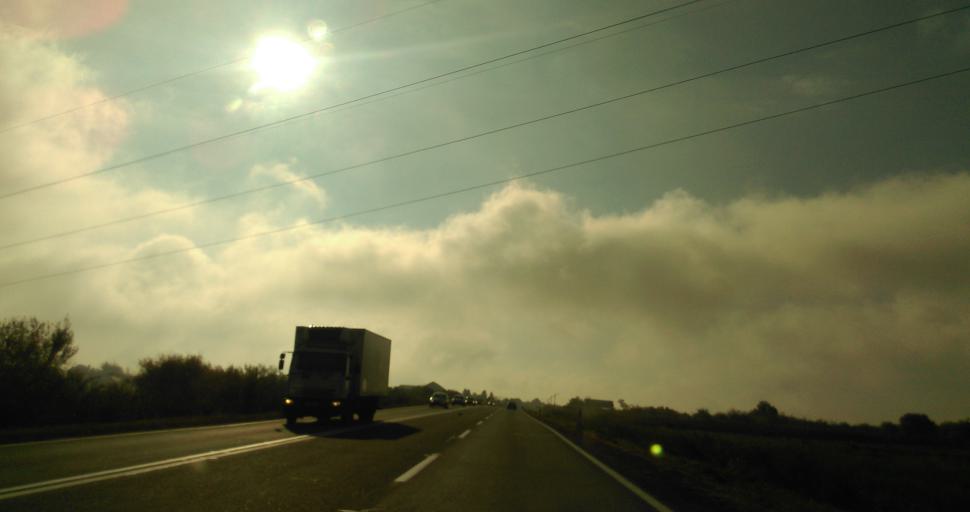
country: RS
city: Rusanj
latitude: 44.6881
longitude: 20.4229
